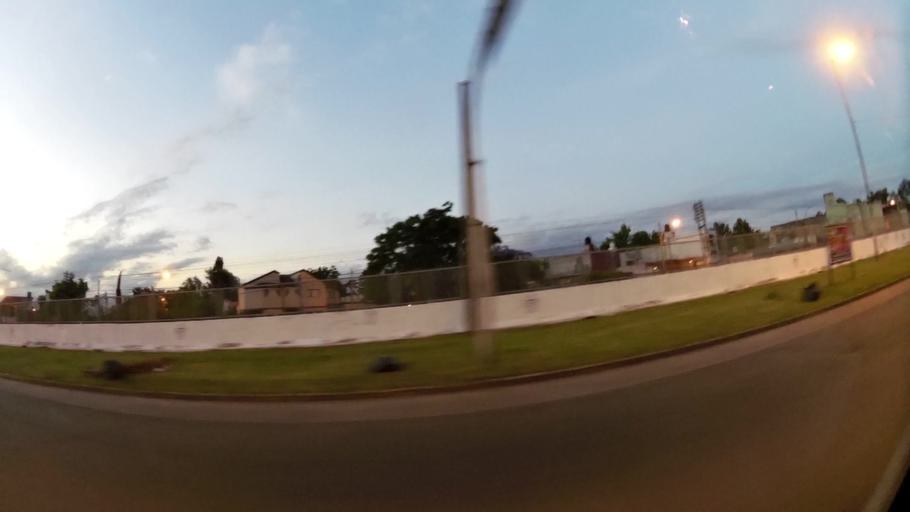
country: AR
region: Buenos Aires
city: Ituzaingo
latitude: -34.6634
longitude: -58.6799
